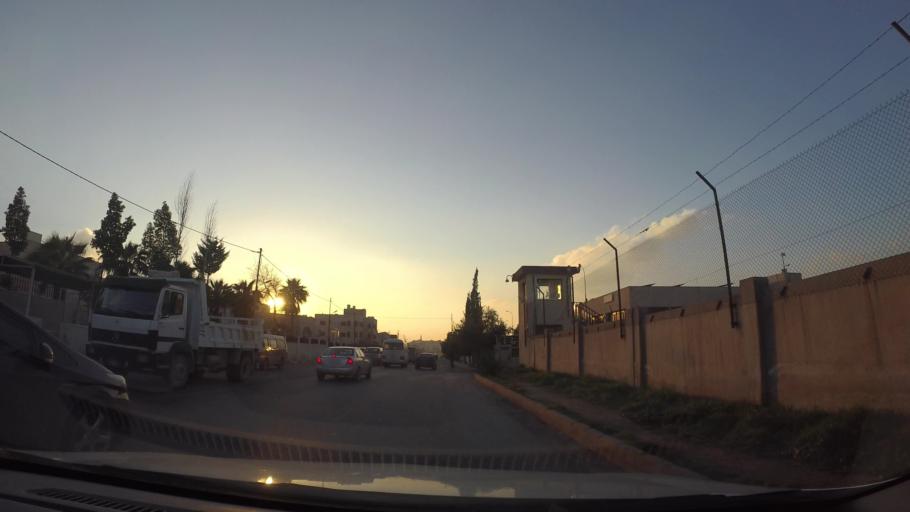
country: JO
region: Amman
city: Al Quwaysimah
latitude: 31.9025
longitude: 35.9301
